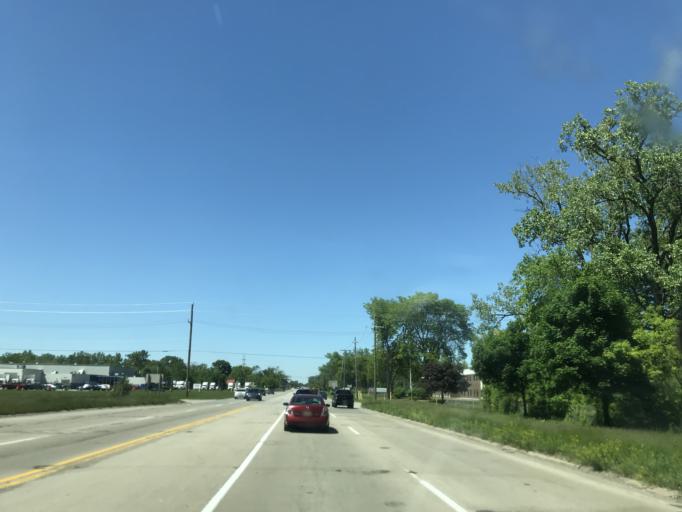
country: US
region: Michigan
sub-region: Wayne County
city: Inkster
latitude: 42.2452
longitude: -83.3281
